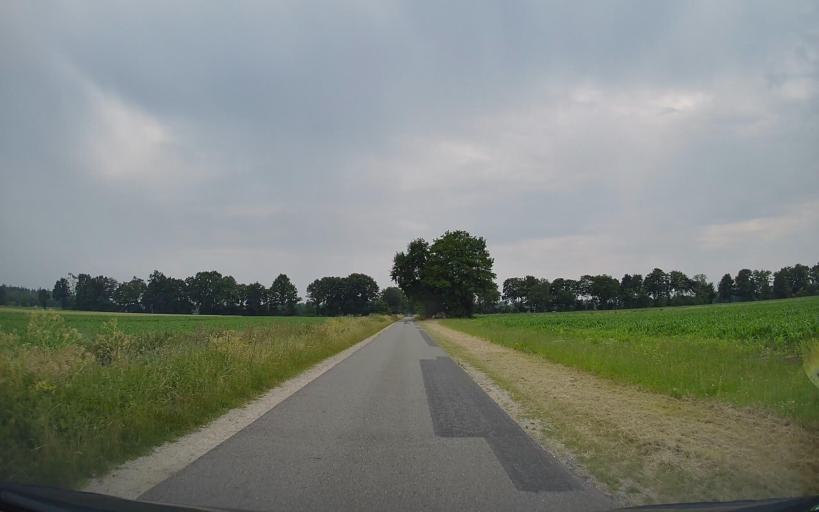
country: DE
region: Lower Saxony
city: Friesoythe
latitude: 53.0100
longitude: 7.8942
